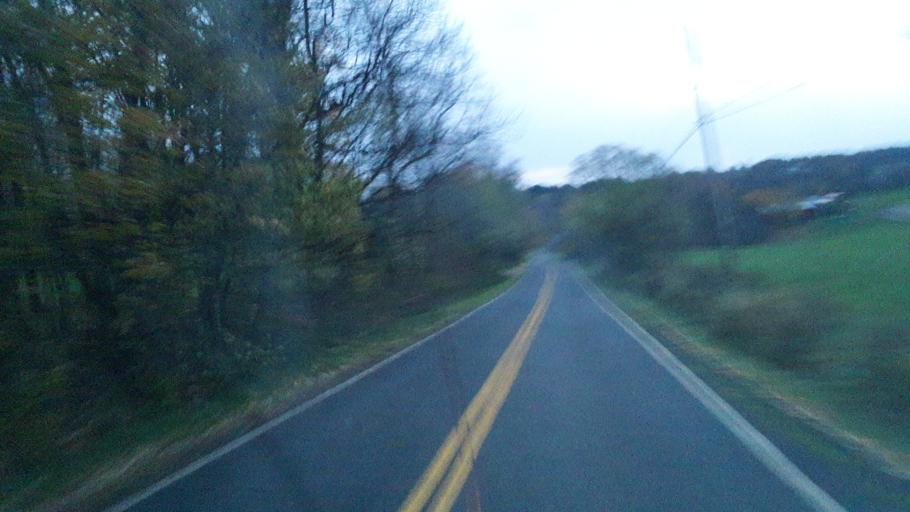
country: US
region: Ohio
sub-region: Portage County
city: Mantua
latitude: 41.2987
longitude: -81.2564
